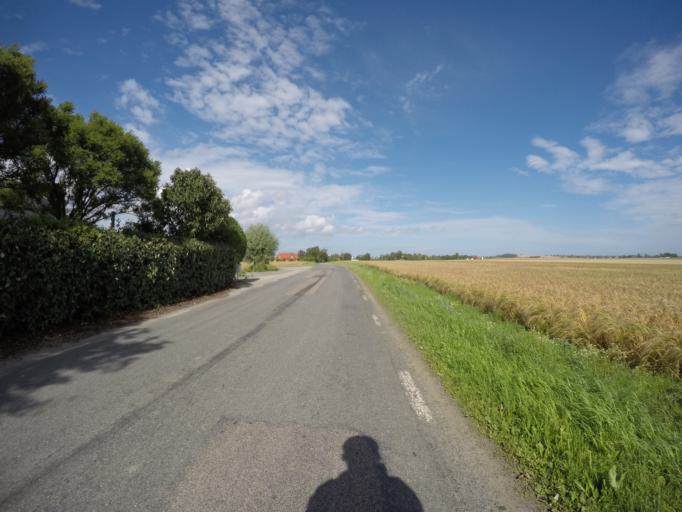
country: SE
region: Skane
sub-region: Simrishamns Kommun
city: Simrishamn
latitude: 55.4928
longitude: 14.1970
